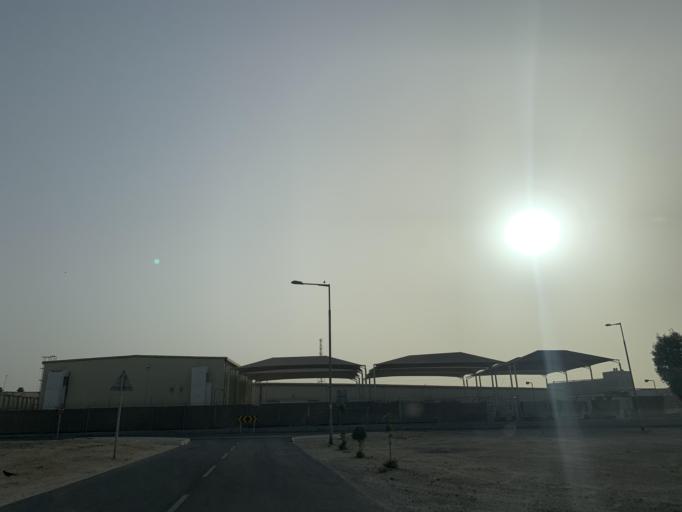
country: BH
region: Manama
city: Manama
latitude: 26.2055
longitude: 50.6046
